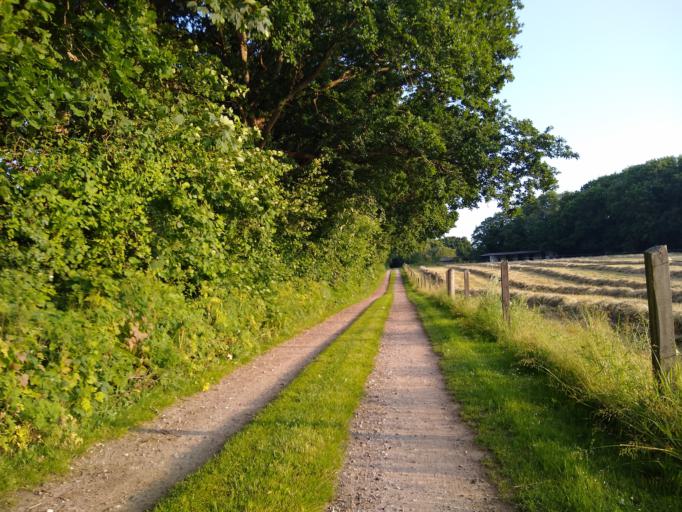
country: DK
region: South Denmark
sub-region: Fredericia Kommune
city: Fredericia
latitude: 55.6226
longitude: 9.8310
